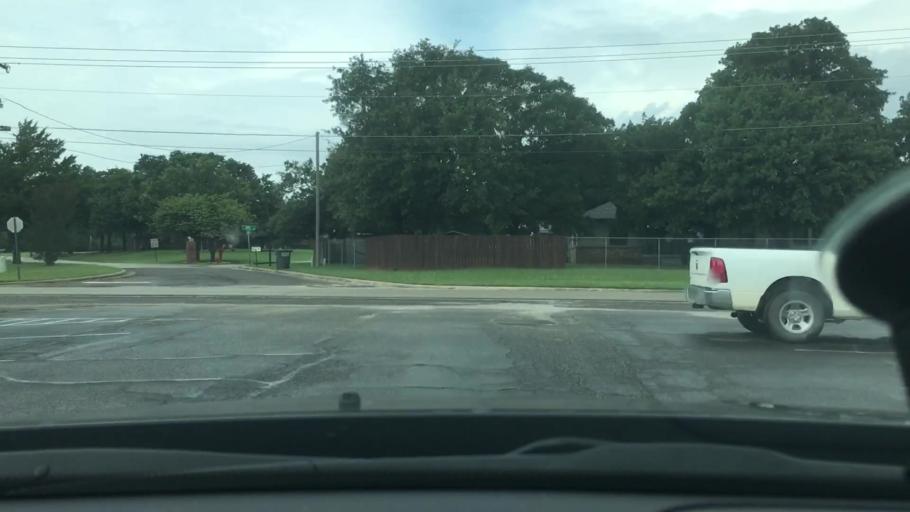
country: US
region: Oklahoma
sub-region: Carter County
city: Healdton
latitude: 34.2232
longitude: -97.4919
